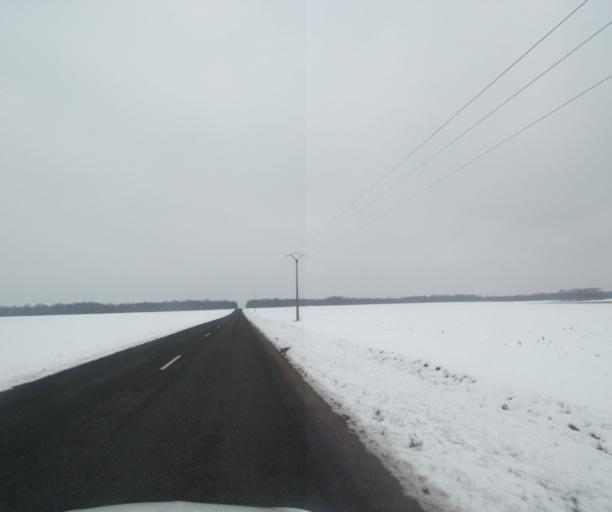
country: FR
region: Champagne-Ardenne
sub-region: Departement de la Haute-Marne
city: Villiers-en-Lieu
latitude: 48.6025
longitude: 4.8779
